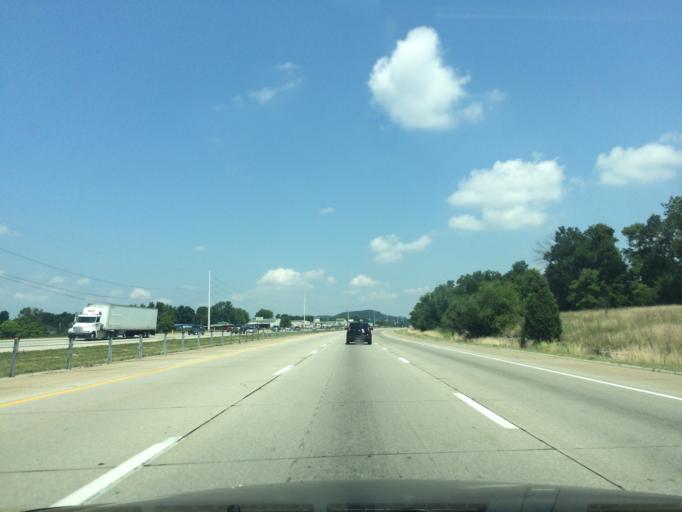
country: US
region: Kentucky
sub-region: Bullitt County
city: Brooks
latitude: 38.0465
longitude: -85.6975
